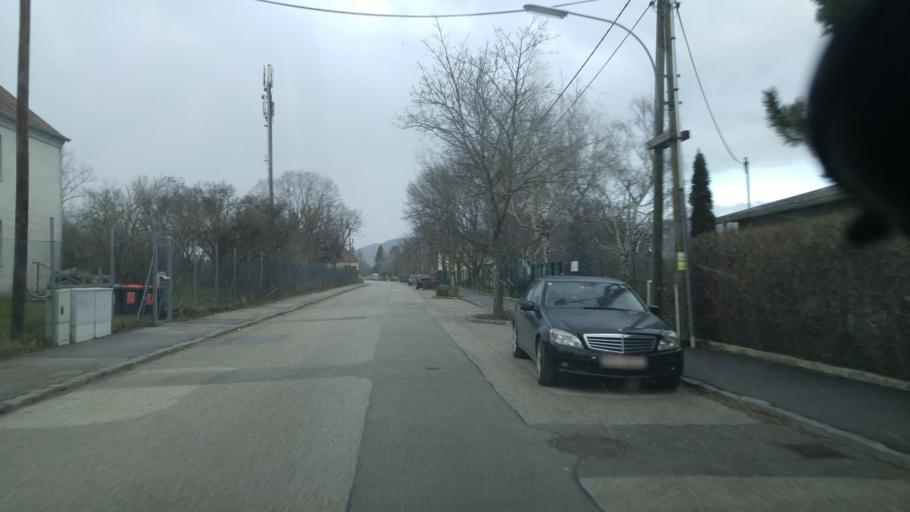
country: AT
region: Lower Austria
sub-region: Politischer Bezirk Baden
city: Baden
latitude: 47.9947
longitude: 16.2253
